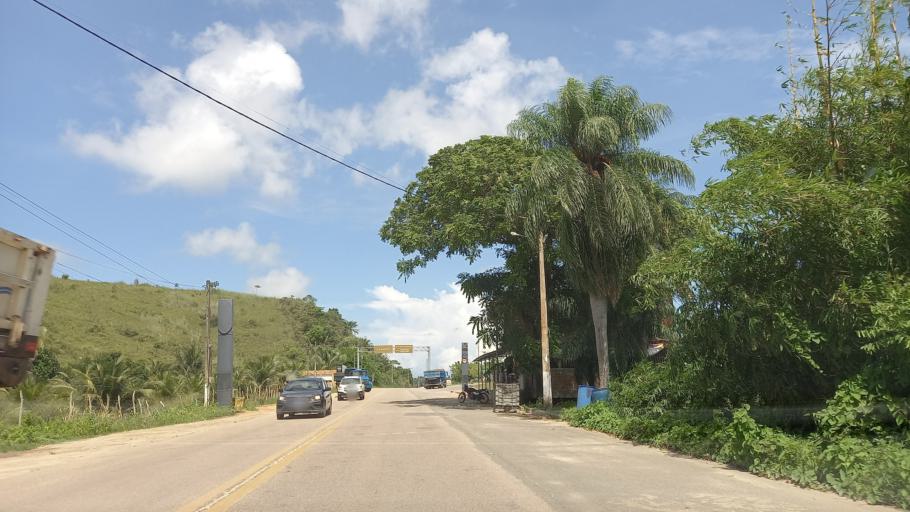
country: BR
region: Pernambuco
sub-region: Barreiros
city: Barreiros
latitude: -8.8055
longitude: -35.1864
